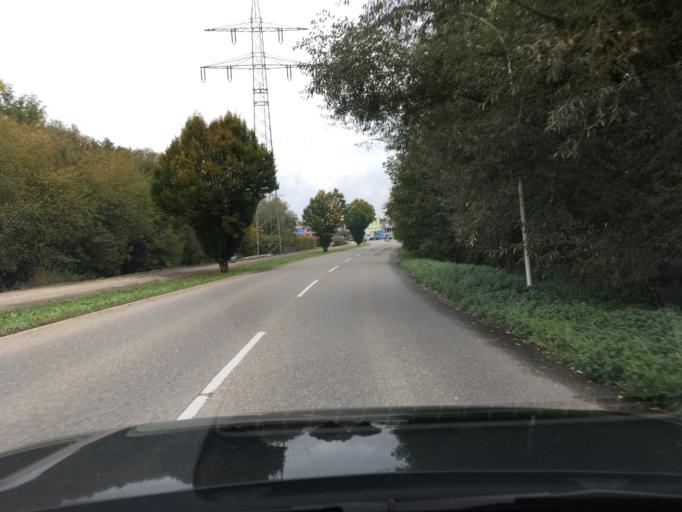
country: DE
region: Baden-Wuerttemberg
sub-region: Tuebingen Region
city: Ofterdingen
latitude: 48.4063
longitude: 9.0356
